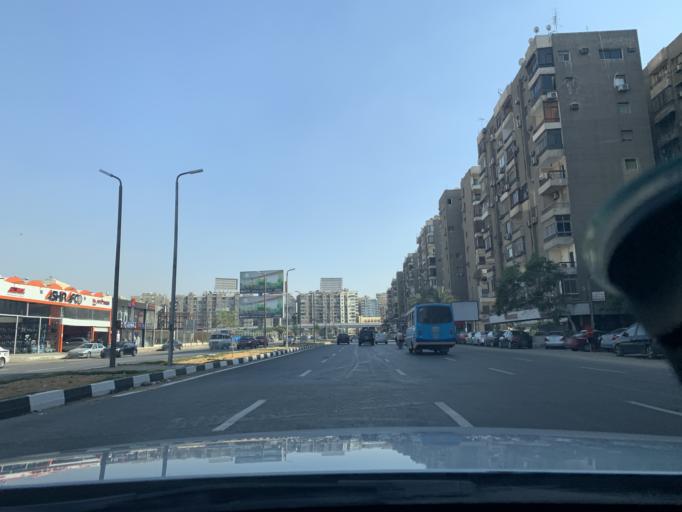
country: EG
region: Muhafazat al Qahirah
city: Cairo
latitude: 30.0726
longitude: 31.3388
